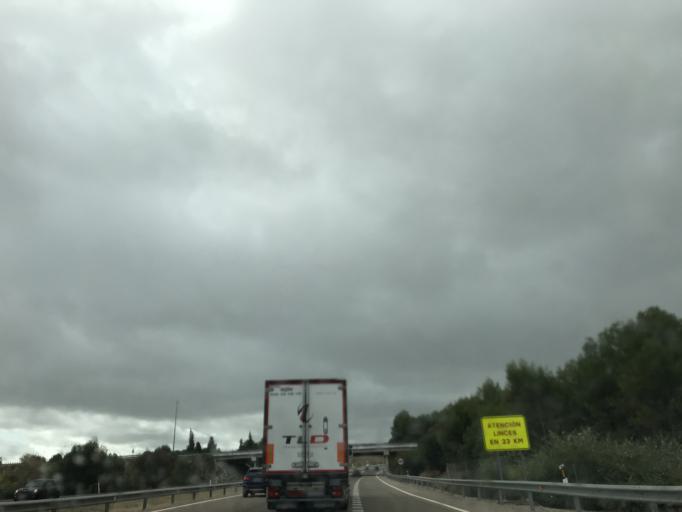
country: ES
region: Andalusia
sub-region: Provincia de Jaen
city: Bailen
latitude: 38.1220
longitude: -3.7594
